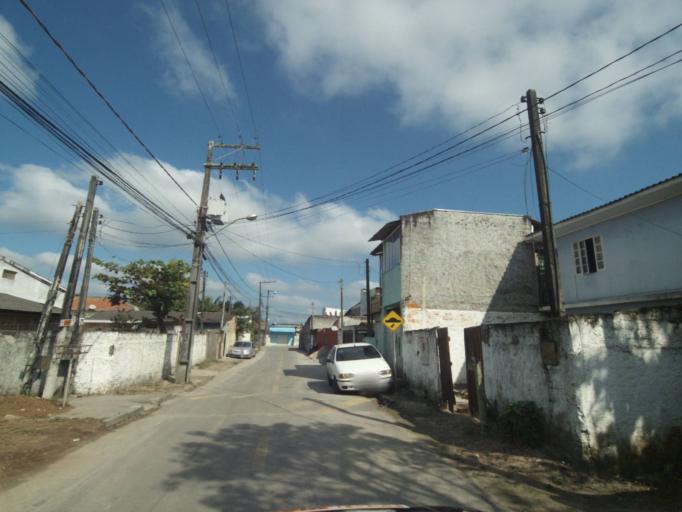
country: BR
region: Parana
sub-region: Paranagua
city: Paranagua
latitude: -25.5265
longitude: -48.5087
